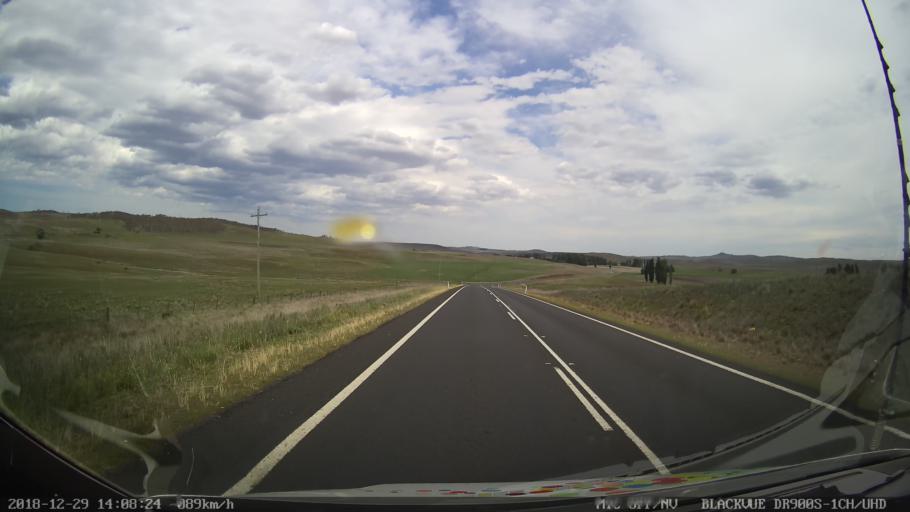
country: AU
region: New South Wales
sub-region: Cooma-Monaro
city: Cooma
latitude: -36.3647
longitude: 149.2145
